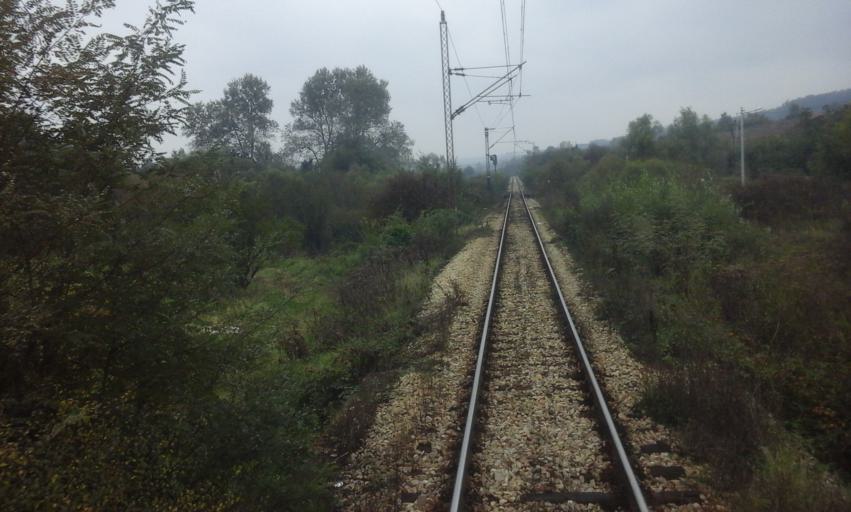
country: RS
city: Rusanj
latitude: 44.6362
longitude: 20.5335
